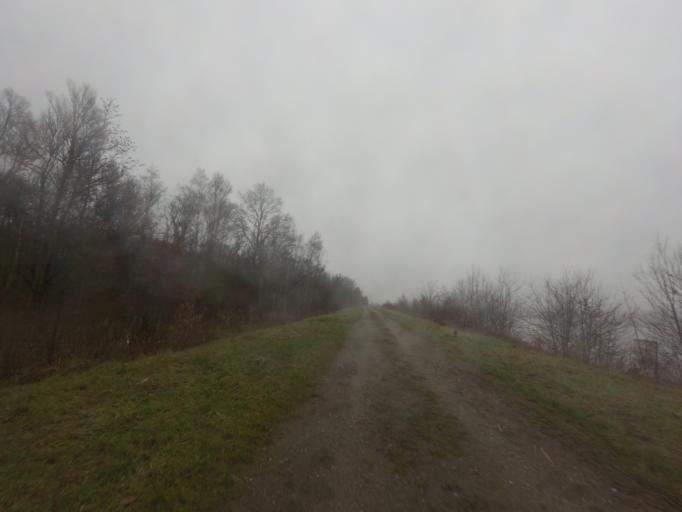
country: BE
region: Flanders
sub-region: Provincie Antwerpen
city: Hoboken
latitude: 51.1908
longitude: 4.3366
